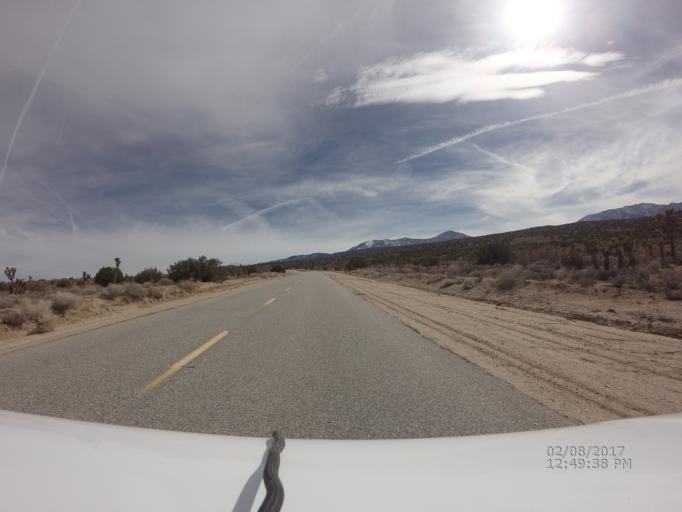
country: US
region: California
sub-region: Los Angeles County
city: Lake Los Angeles
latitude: 34.4698
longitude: -117.8280
